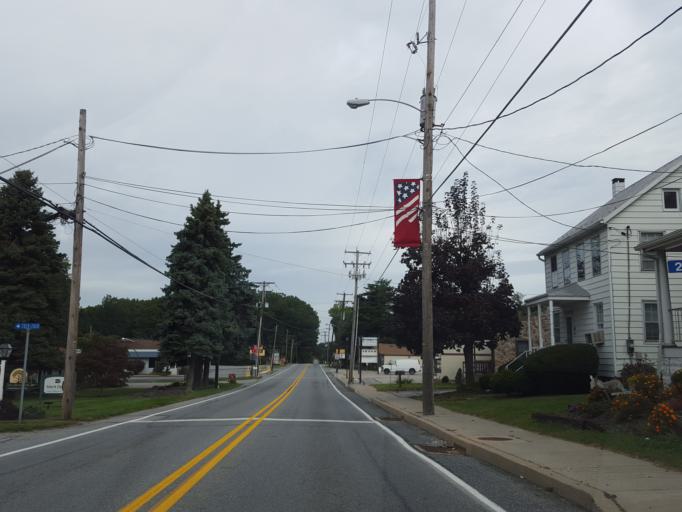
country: US
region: Pennsylvania
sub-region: York County
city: West York
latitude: 39.9075
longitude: -76.7908
